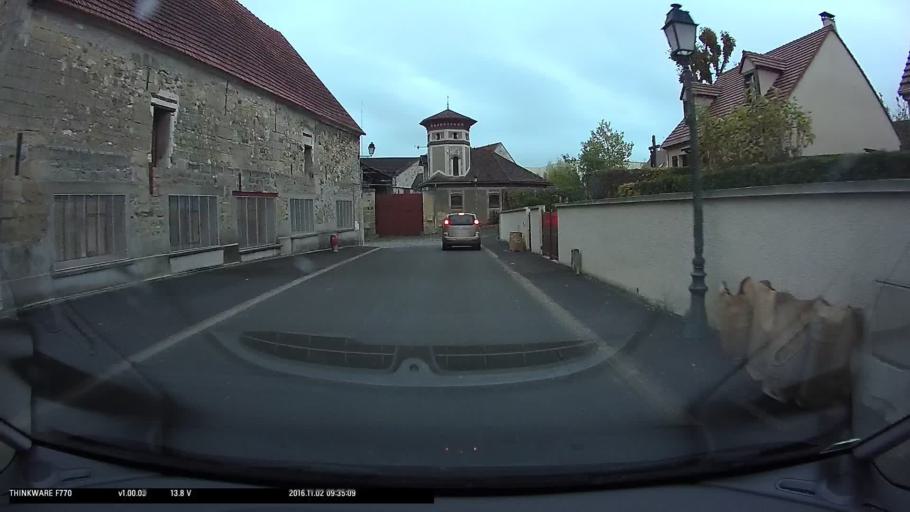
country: FR
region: Ile-de-France
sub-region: Departement du Val-d'Oise
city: Courdimanche
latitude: 49.0573
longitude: 2.0180
